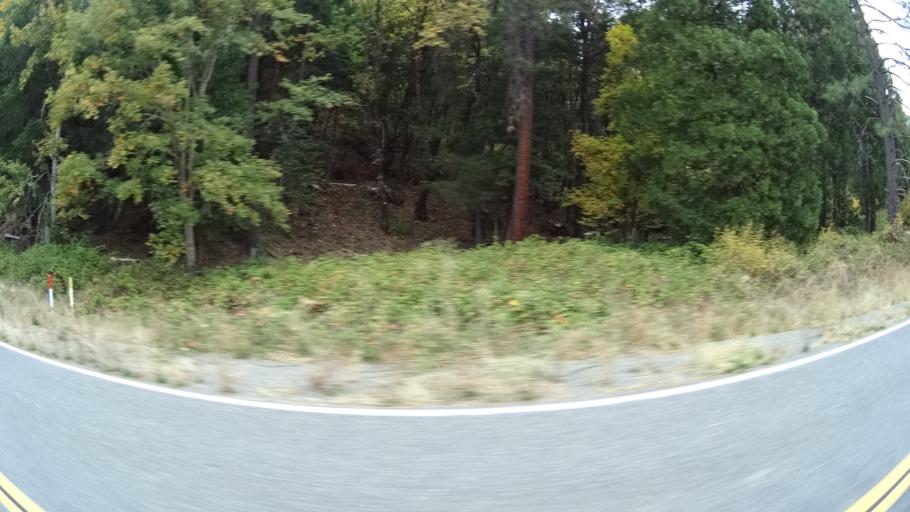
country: US
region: California
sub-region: Siskiyou County
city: Happy Camp
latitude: 41.8759
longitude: -123.4154
